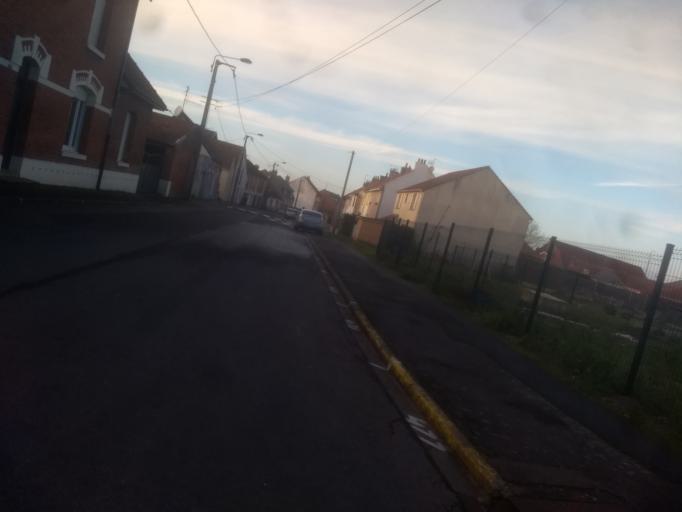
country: FR
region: Nord-Pas-de-Calais
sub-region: Departement du Pas-de-Calais
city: Beaurains
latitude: 50.2614
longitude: 2.7898
